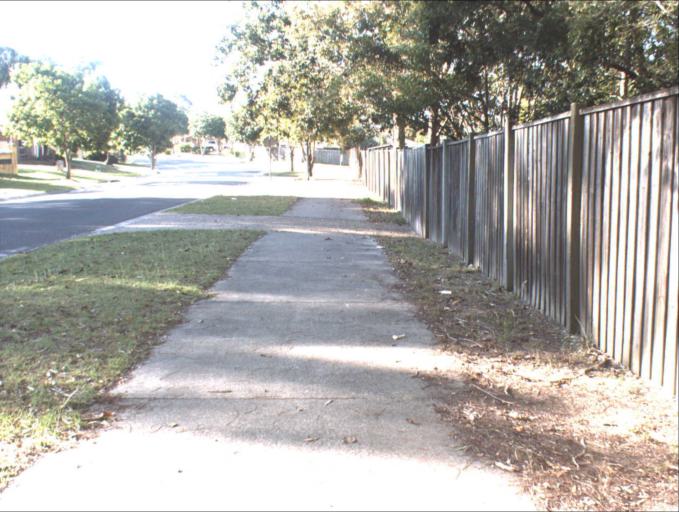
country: AU
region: Queensland
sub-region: Logan
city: Park Ridge South
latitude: -27.6981
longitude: 153.0216
